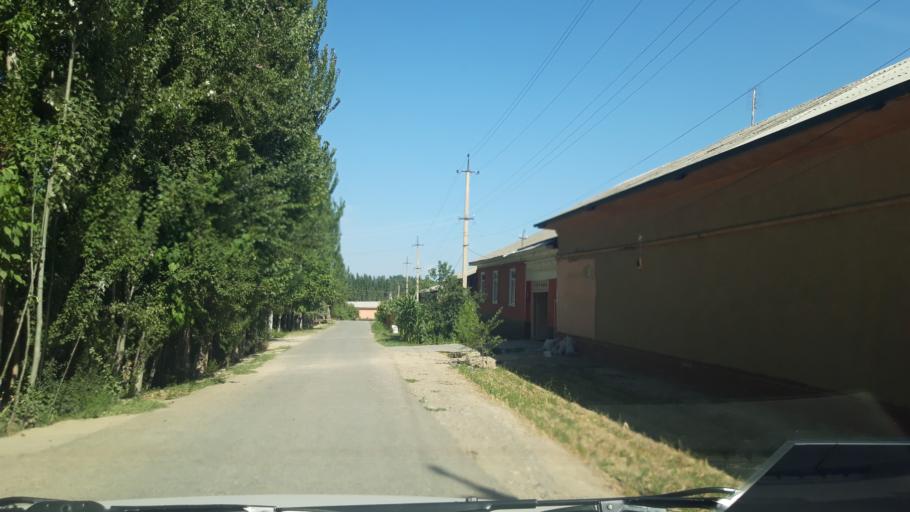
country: UZ
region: Namangan
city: Yangiqo`rg`on
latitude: 41.2026
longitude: 71.7226
